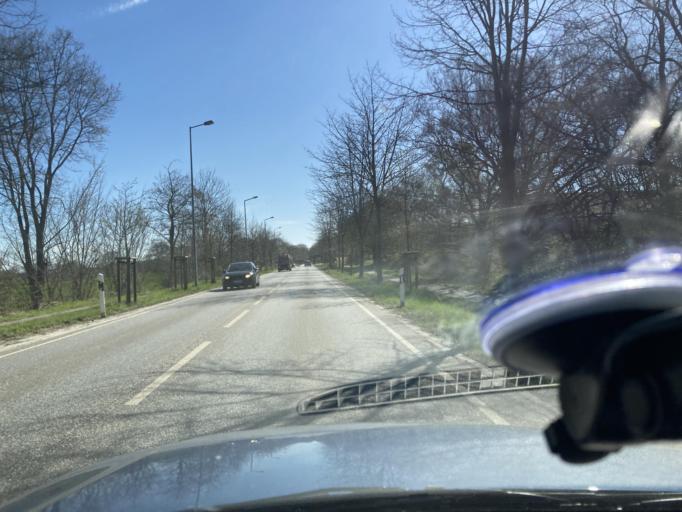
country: DE
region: Schleswig-Holstein
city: Ostrohe
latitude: 54.1975
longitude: 9.1307
